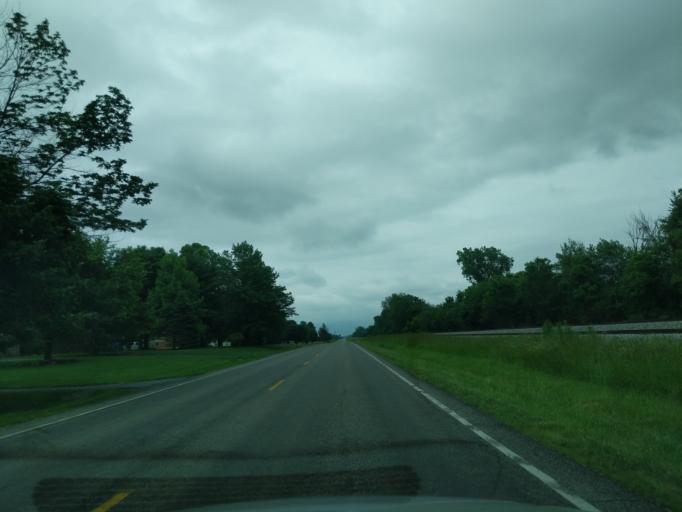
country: US
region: Indiana
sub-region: Madison County
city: Elwood
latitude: 40.2815
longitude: -85.9286
